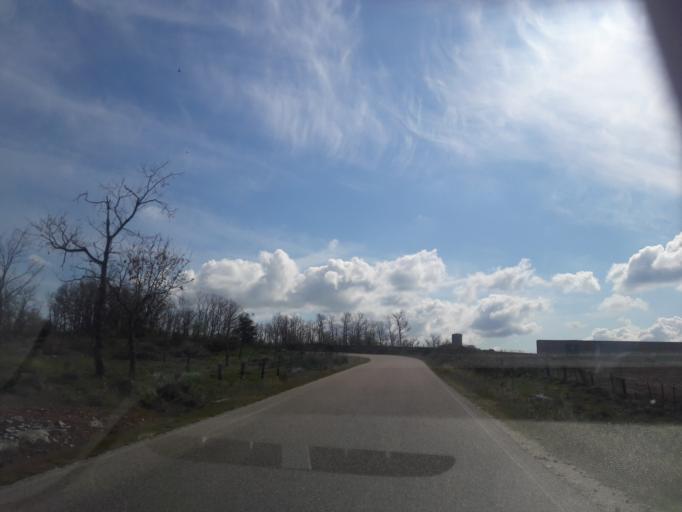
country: ES
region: Castille and Leon
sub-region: Provincia de Salamanca
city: Valdefuentes de Sangusin
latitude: 40.5187
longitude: -5.8508
